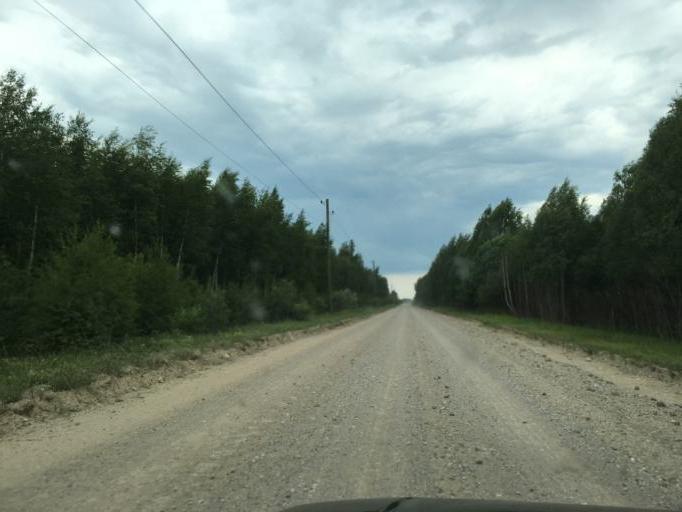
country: LV
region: Lubana
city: Lubana
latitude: 56.8247
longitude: 26.8811
